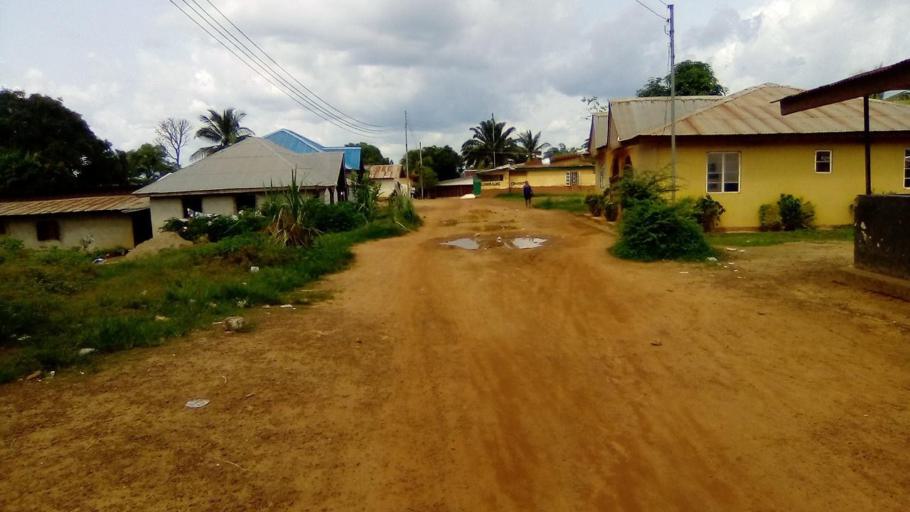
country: SL
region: Southern Province
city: Bo
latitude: 7.9606
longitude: -11.7222
